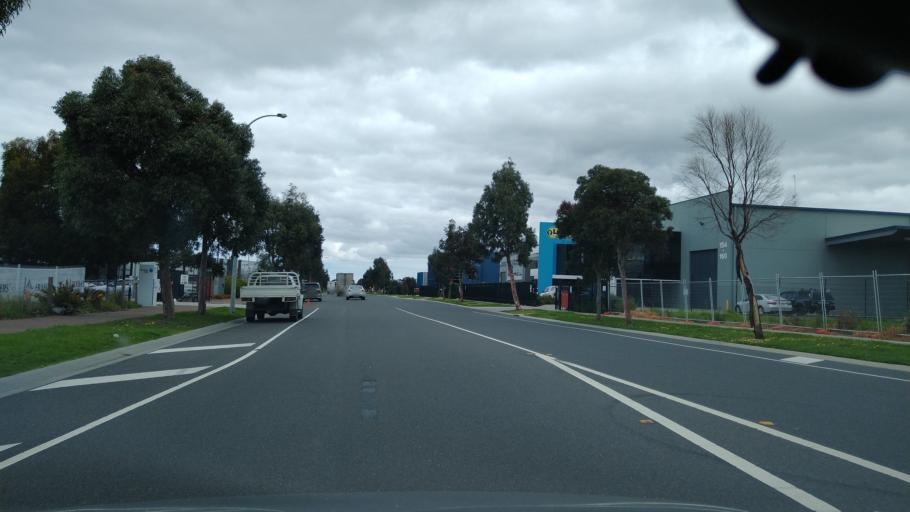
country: AU
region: Victoria
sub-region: Frankston
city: Sandhurst
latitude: -38.0498
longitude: 145.2168
